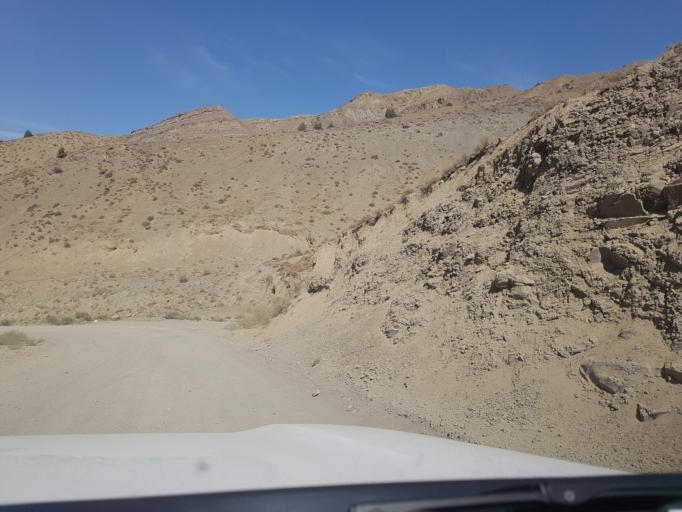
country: TM
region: Ahal
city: Baharly
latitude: 38.4453
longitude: 57.0490
